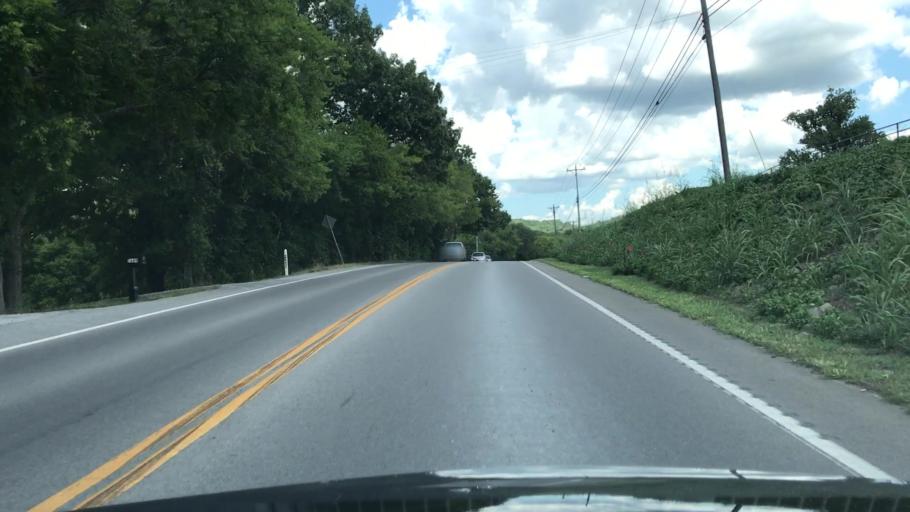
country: US
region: Tennessee
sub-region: Williamson County
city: Nolensville
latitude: 35.8982
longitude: -86.6665
